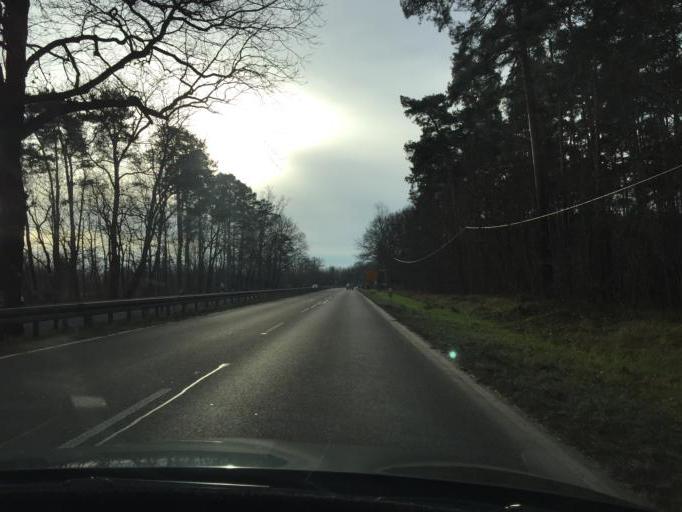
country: DE
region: Brandenburg
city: Peitz
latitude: 51.8003
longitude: 14.3818
